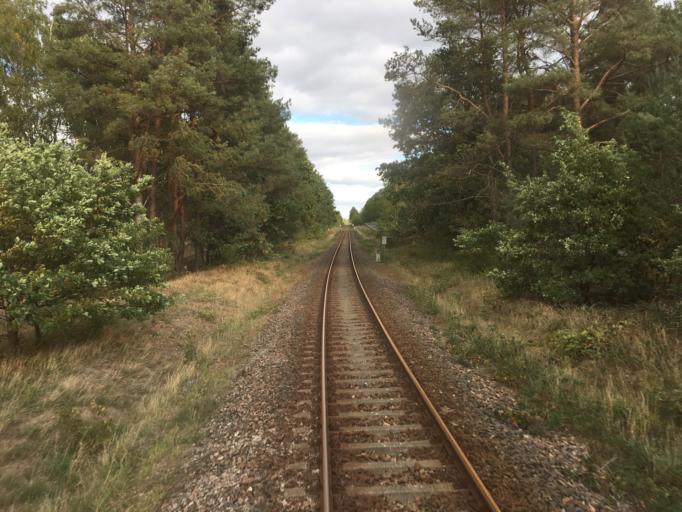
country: DE
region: Mecklenburg-Vorpommern
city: Malchow
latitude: 53.5294
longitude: 12.4662
